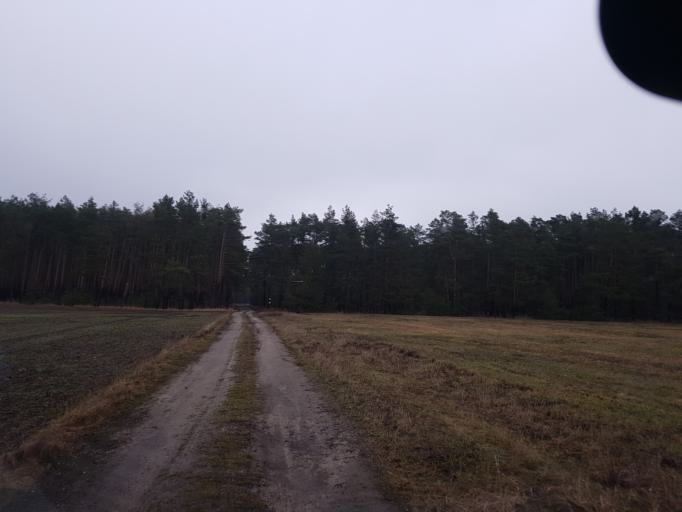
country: DE
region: Brandenburg
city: Finsterwalde
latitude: 51.5706
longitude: 13.6836
